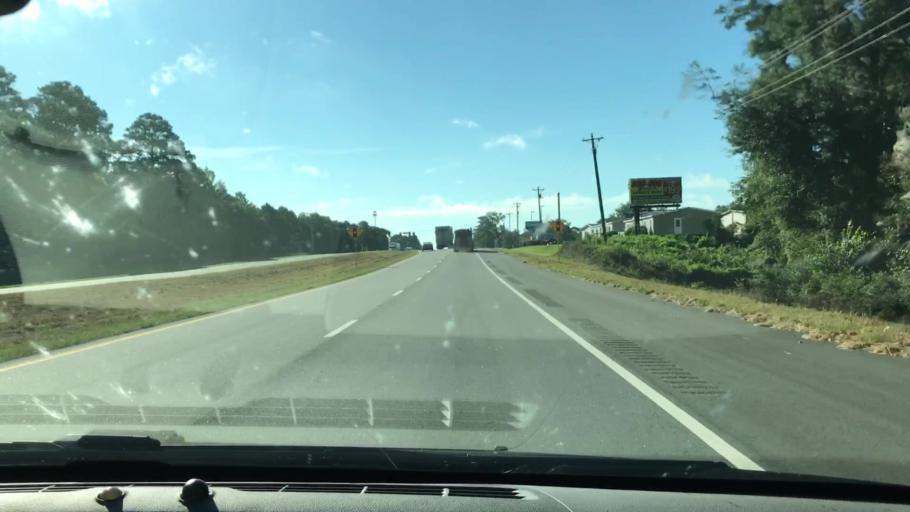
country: US
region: Georgia
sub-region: Lee County
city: Leesburg
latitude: 31.6656
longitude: -84.2822
